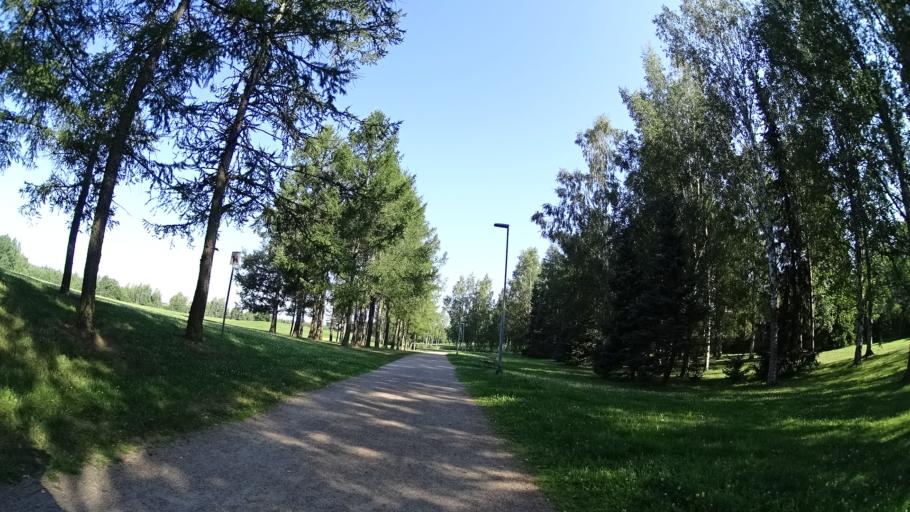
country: FI
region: Uusimaa
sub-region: Helsinki
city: Vantaa
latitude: 60.2756
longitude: 24.9858
